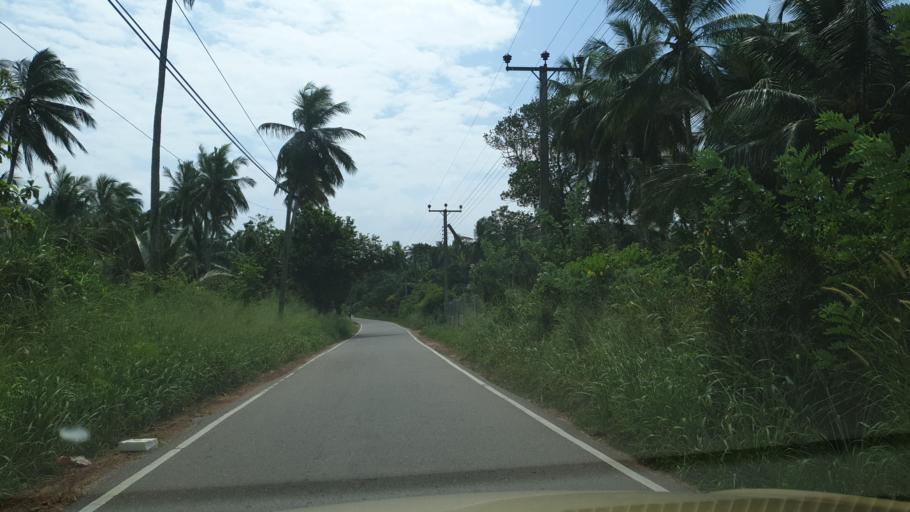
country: LK
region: North Western
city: Kuliyapitiya
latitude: 7.3513
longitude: 79.9783
